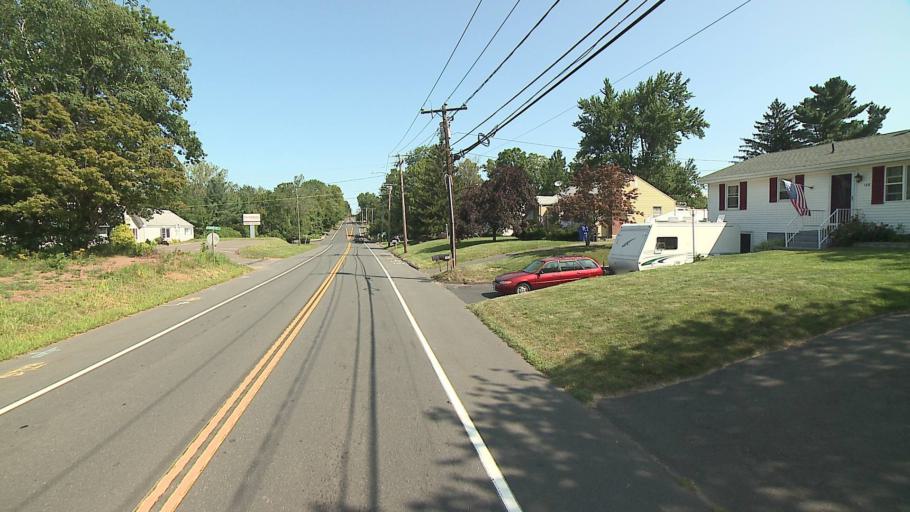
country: US
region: Connecticut
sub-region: Hartford County
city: Windsor Locks
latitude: 41.9354
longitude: -72.6040
